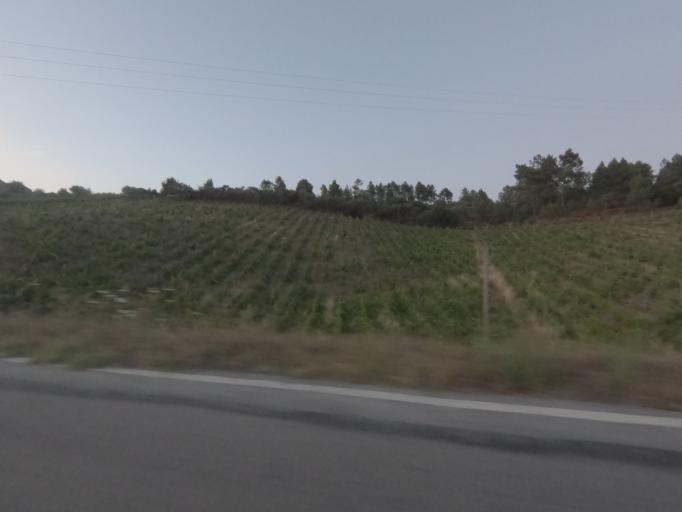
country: PT
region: Viseu
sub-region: Armamar
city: Armamar
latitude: 41.2014
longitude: -7.6985
